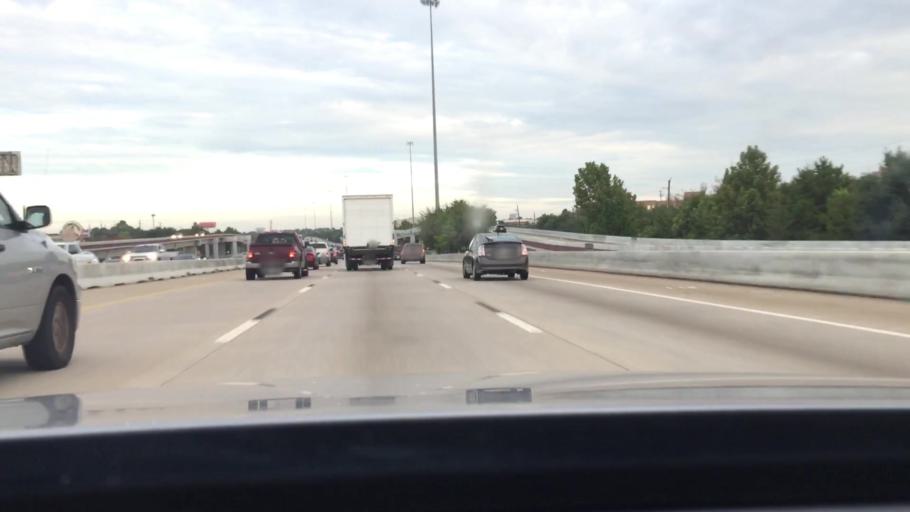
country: US
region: Texas
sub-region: Harris County
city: Hudson
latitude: 29.9618
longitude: -95.5486
